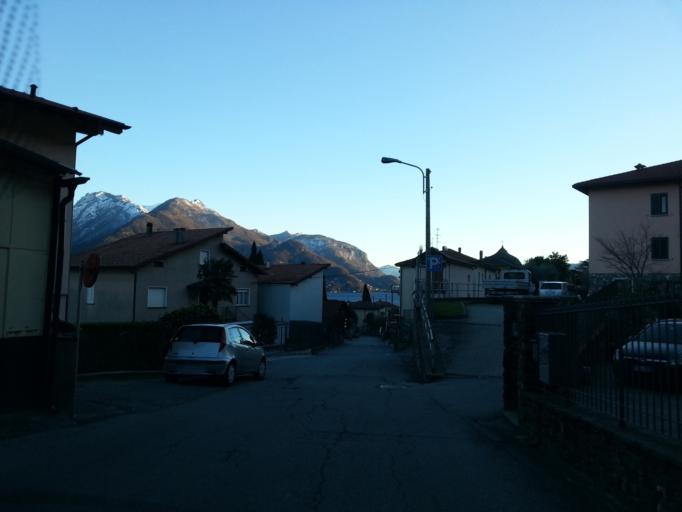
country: IT
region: Lombardy
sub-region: Provincia di Como
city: San Siro
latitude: 46.0648
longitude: 9.2669
